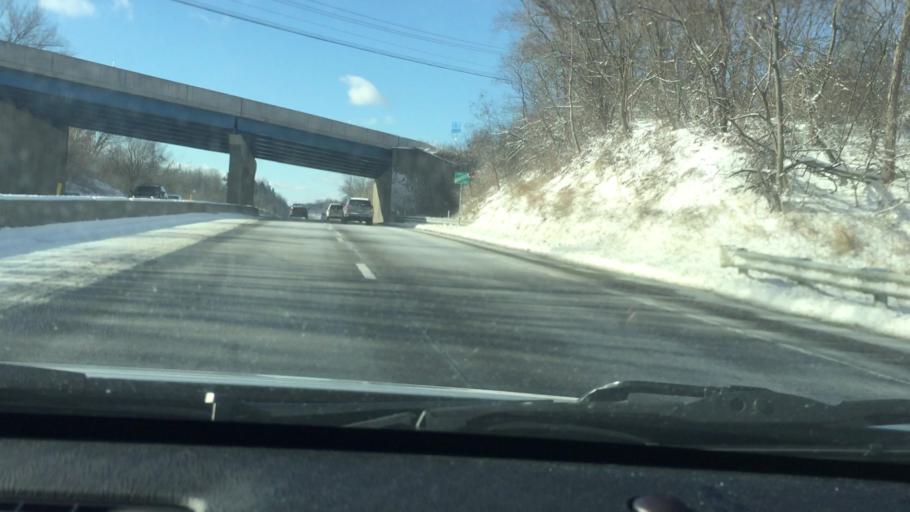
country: US
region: Pennsylvania
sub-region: Allegheny County
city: Oakdale
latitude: 40.4444
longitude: -80.1778
